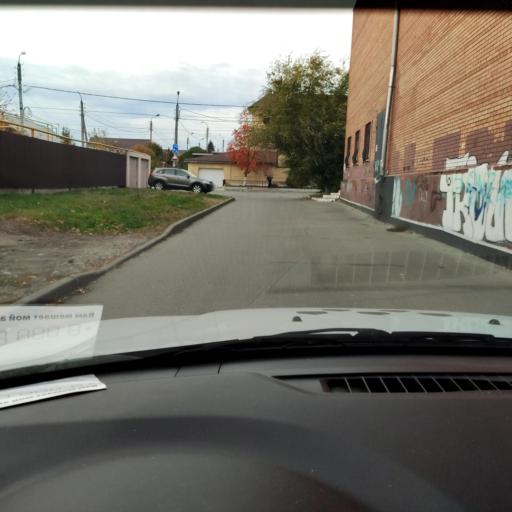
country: RU
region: Samara
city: Tol'yatti
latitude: 53.5328
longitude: 49.3925
